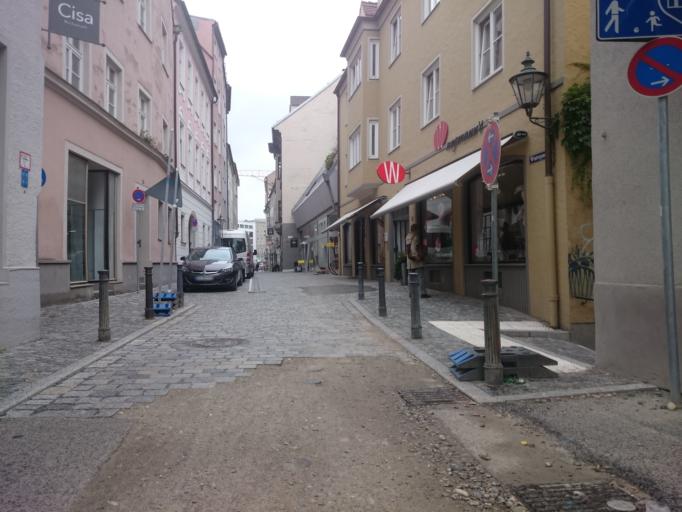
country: DE
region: Bavaria
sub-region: Swabia
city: Augsburg
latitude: 48.3660
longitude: 10.8999
